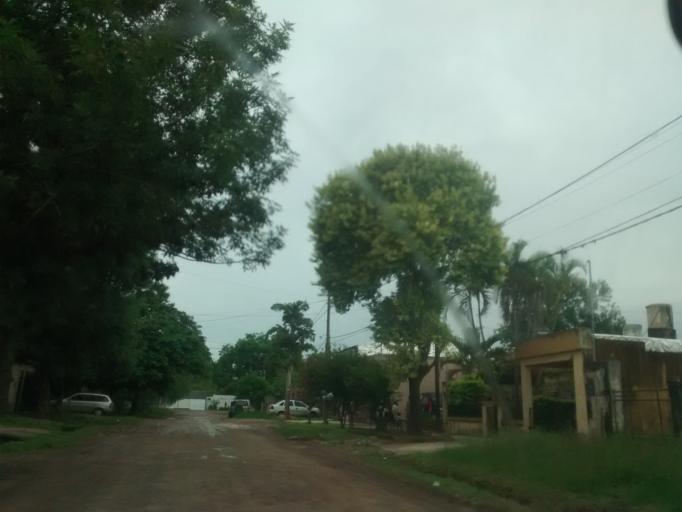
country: AR
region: Chaco
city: Resistencia
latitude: -27.4389
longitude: -58.9797
